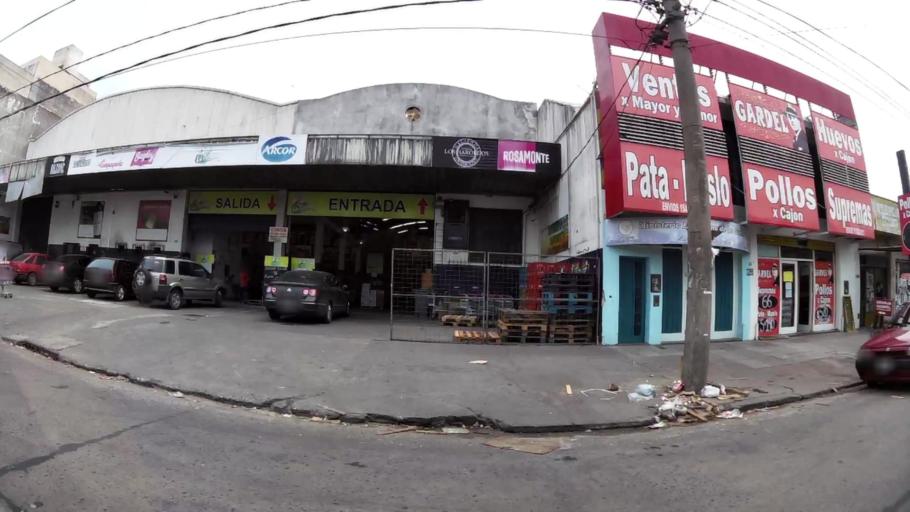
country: AR
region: Buenos Aires
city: San Justo
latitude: -34.6864
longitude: -58.5206
